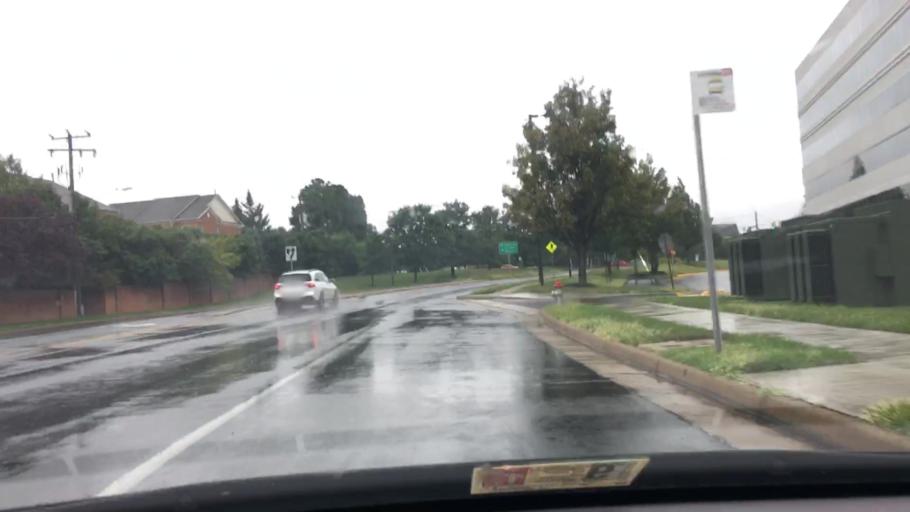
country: US
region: Virginia
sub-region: Fairfax County
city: Tysons Corner
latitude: 38.9168
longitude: -77.2378
